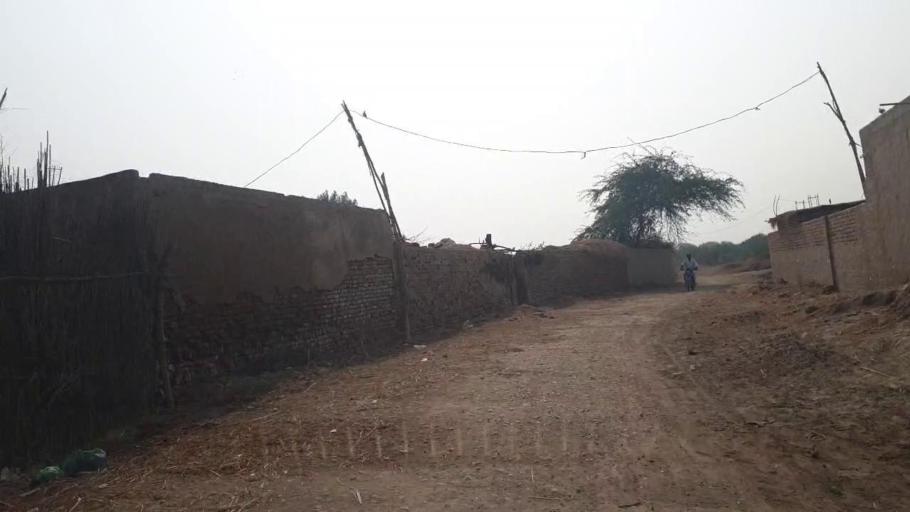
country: PK
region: Sindh
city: Tando Muhammad Khan
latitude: 25.2728
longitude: 68.4914
